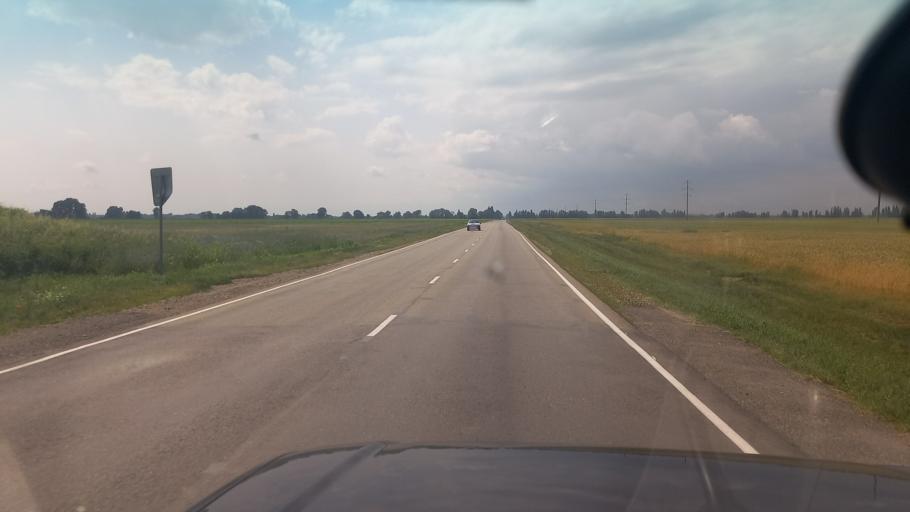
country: RU
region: Adygeya
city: Koshekhabl'
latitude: 44.9057
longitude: 40.4643
